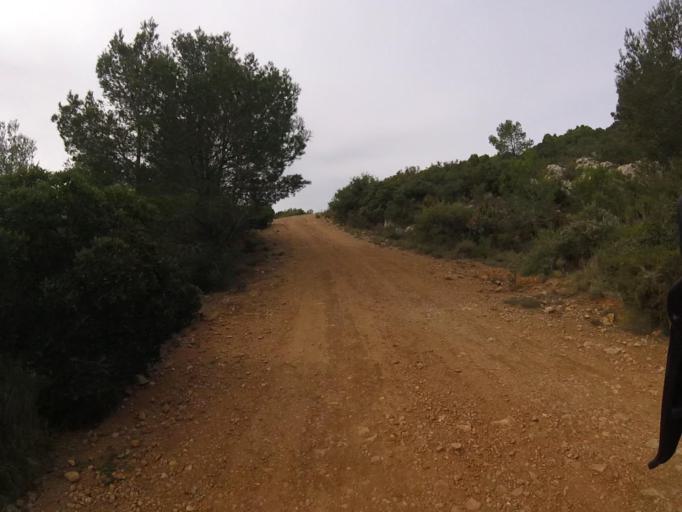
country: ES
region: Valencia
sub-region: Provincia de Castello
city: Benicassim
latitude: 40.0861
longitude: 0.0396
